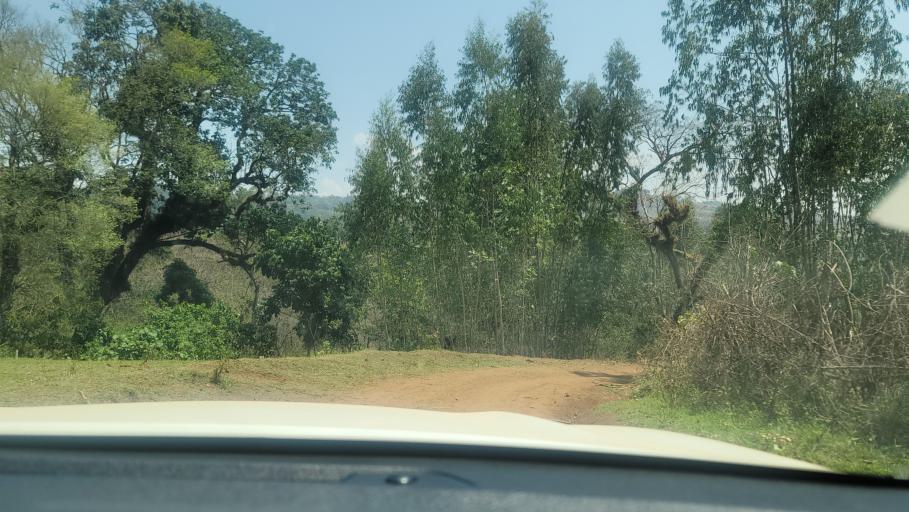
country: ET
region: Southern Nations, Nationalities, and People's Region
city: Bonga
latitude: 7.5284
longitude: 36.1945
